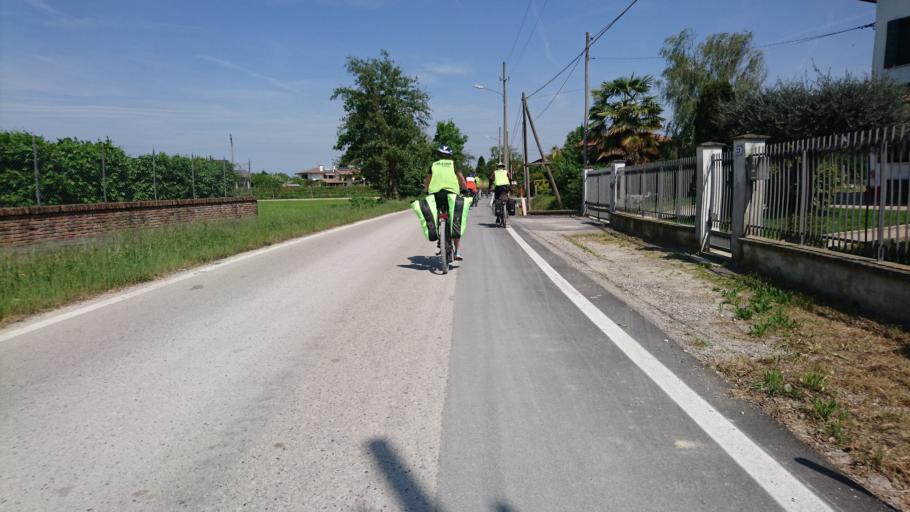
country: IT
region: Veneto
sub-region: Provincia di Padova
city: Vigodarzere
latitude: 45.4444
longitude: 11.8844
